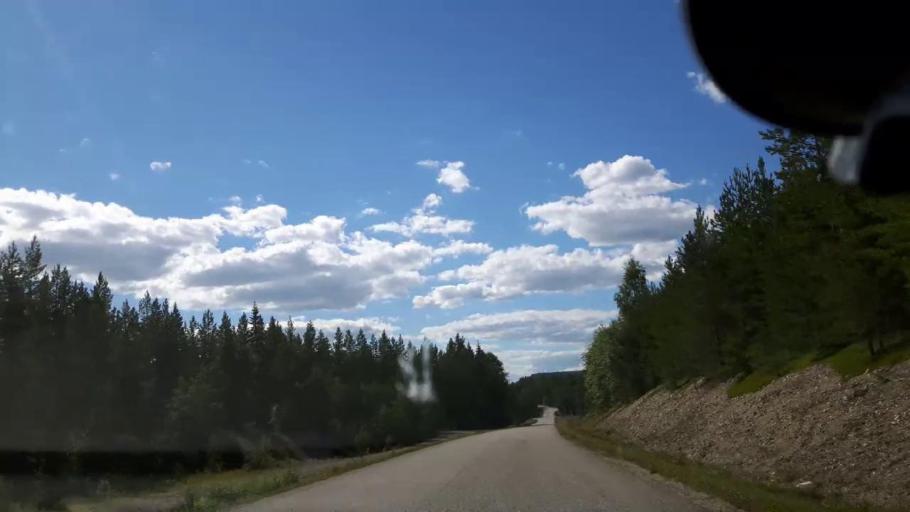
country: SE
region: Vaesternorrland
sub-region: Ange Kommun
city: Fransta
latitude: 62.7799
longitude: 16.0396
